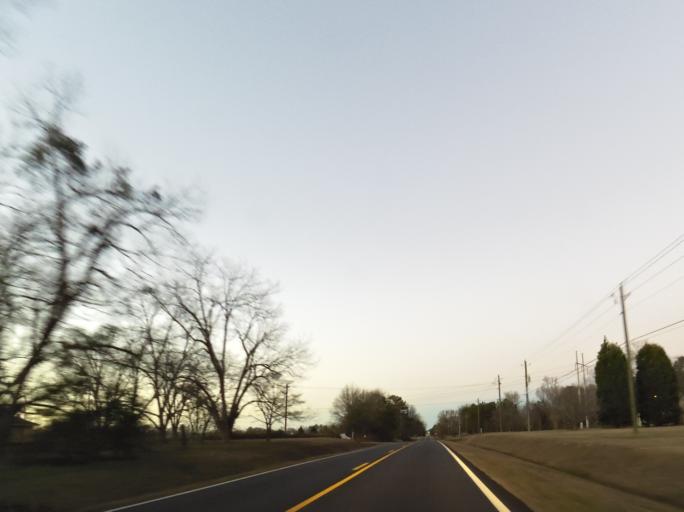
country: US
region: Georgia
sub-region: Peach County
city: Byron
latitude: 32.6343
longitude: -83.7573
